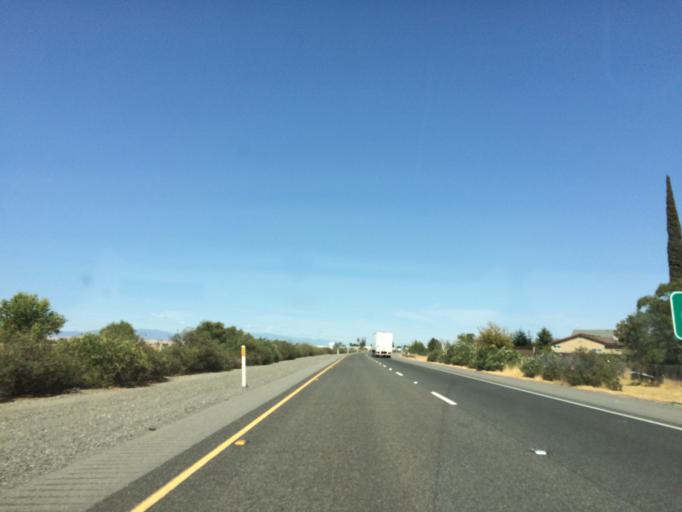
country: US
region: California
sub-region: Glenn County
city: Willows
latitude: 39.5143
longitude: -122.2109
